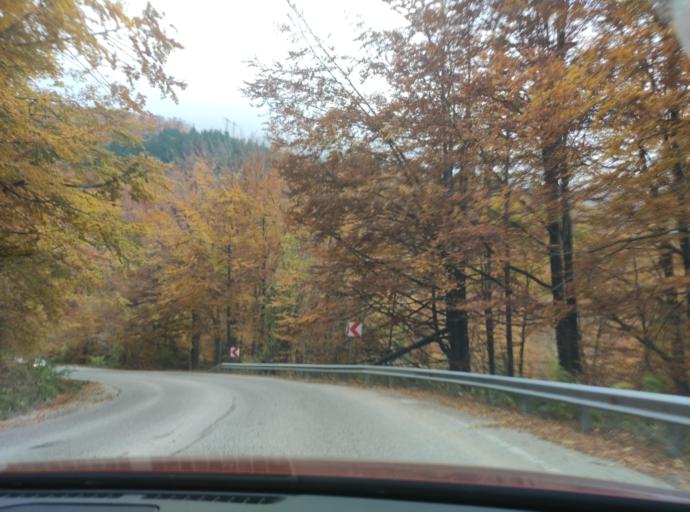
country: BG
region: Montana
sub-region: Obshtina Berkovitsa
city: Berkovitsa
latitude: 43.1349
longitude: 23.1415
